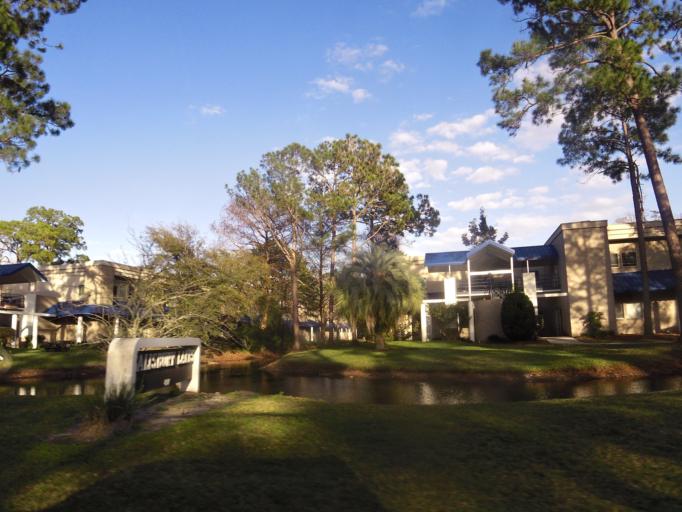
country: US
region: Florida
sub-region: Duval County
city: Jacksonville
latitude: 30.2535
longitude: -81.5948
